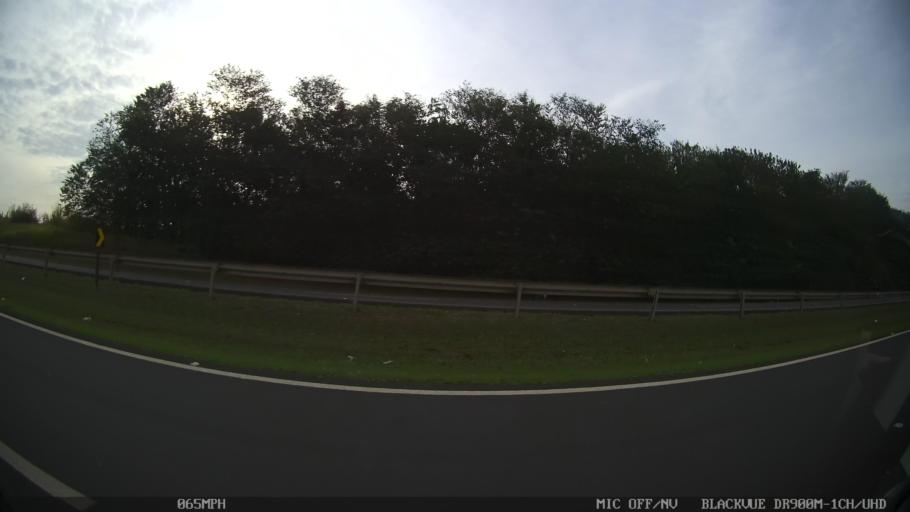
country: BR
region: Sao Paulo
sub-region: Piracicaba
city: Piracicaba
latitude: -22.7003
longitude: -47.5972
